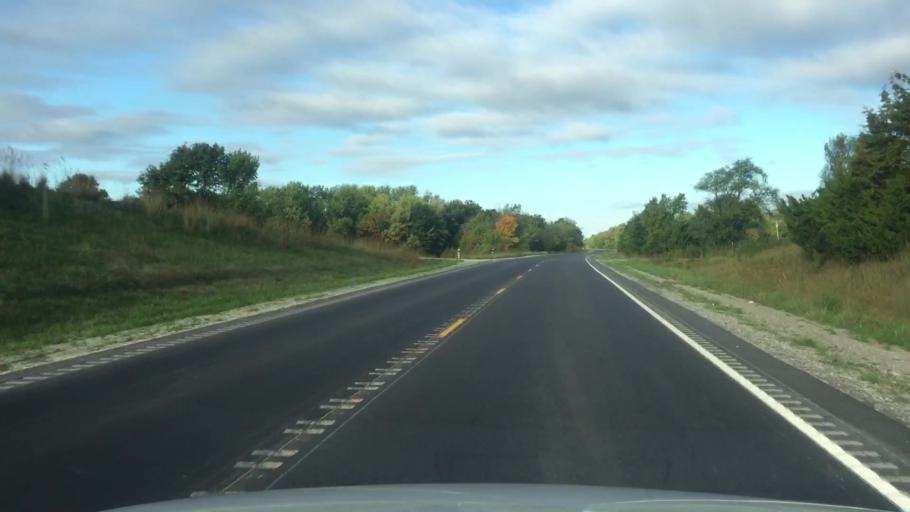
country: US
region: Missouri
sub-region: Boone County
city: Columbia
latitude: 38.9894
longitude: -92.5044
